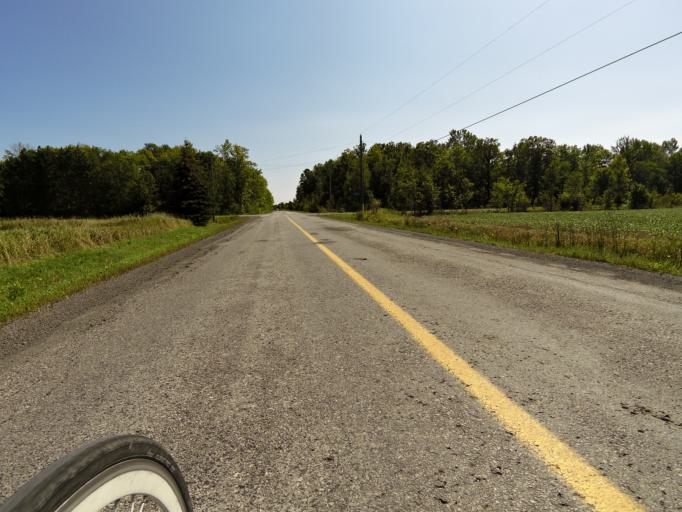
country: CA
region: Ontario
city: Bells Corners
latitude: 45.4341
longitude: -76.0622
